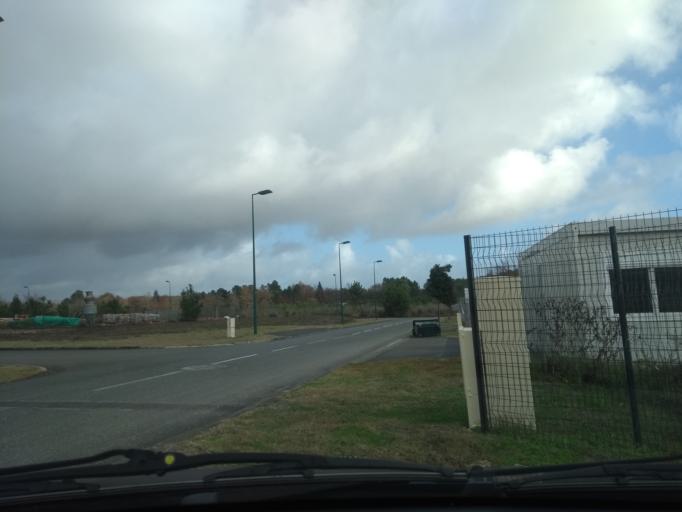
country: FR
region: Aquitaine
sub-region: Departement de la Gironde
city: Belin-Beliet
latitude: 44.5263
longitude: -0.8176
